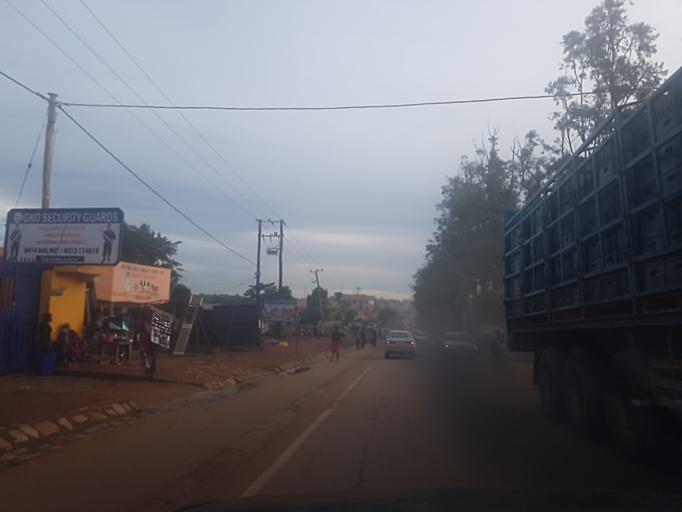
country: UG
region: Central Region
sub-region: Wakiso District
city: Bweyogerere
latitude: 0.3880
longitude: 32.6548
